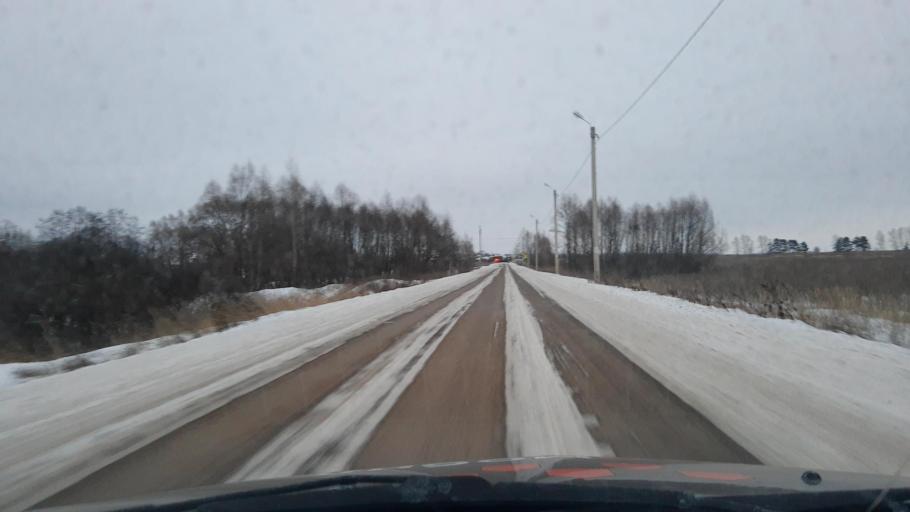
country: RU
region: Bashkortostan
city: Kabakovo
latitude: 54.6476
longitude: 56.1820
